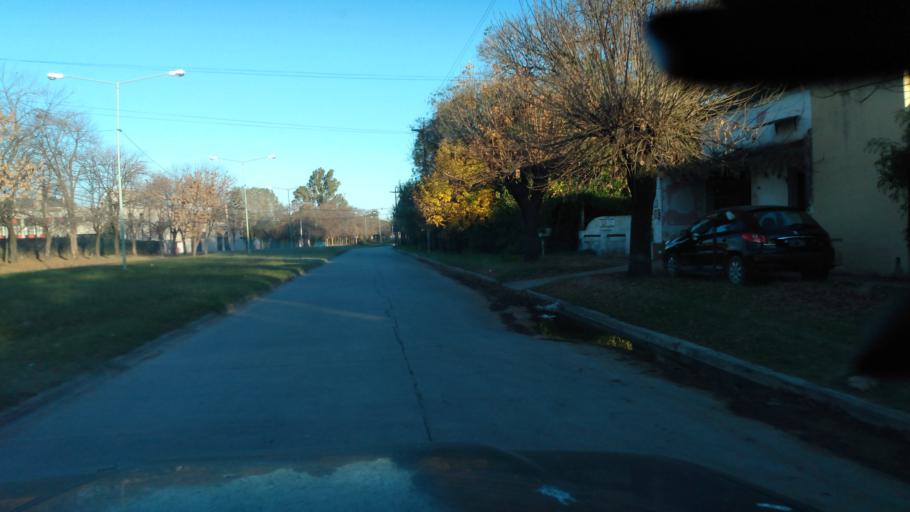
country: AR
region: Buenos Aires
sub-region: Partido de Lujan
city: Lujan
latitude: -34.5612
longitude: -59.1274
